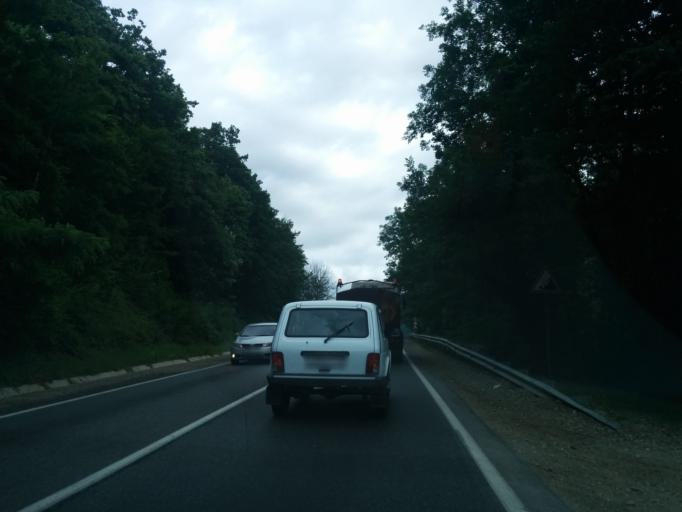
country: RU
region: Krasnodarskiy
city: Agoy
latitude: 44.1310
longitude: 39.0466
